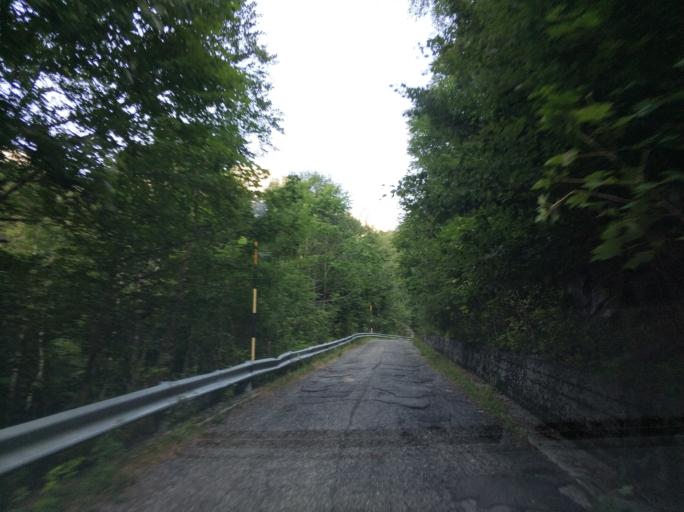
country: IT
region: Piedmont
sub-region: Provincia di Torino
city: Usseglio
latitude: 45.2389
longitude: 7.1943
